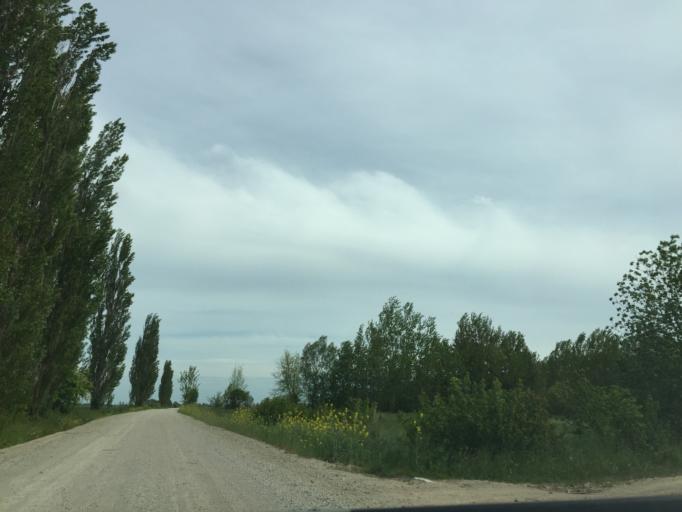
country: LT
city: Linkuva
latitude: 56.0298
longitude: 24.1751
